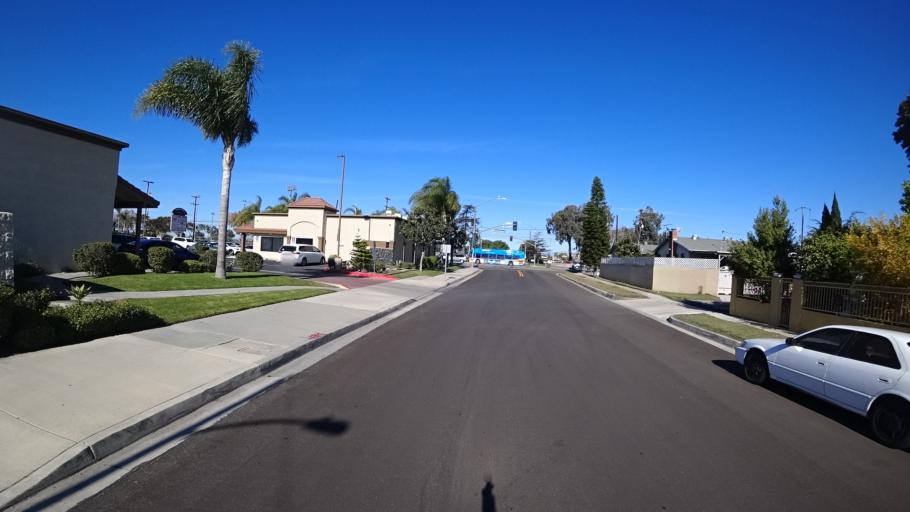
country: US
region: California
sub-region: Orange County
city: Midway City
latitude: 33.7589
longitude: -117.9657
